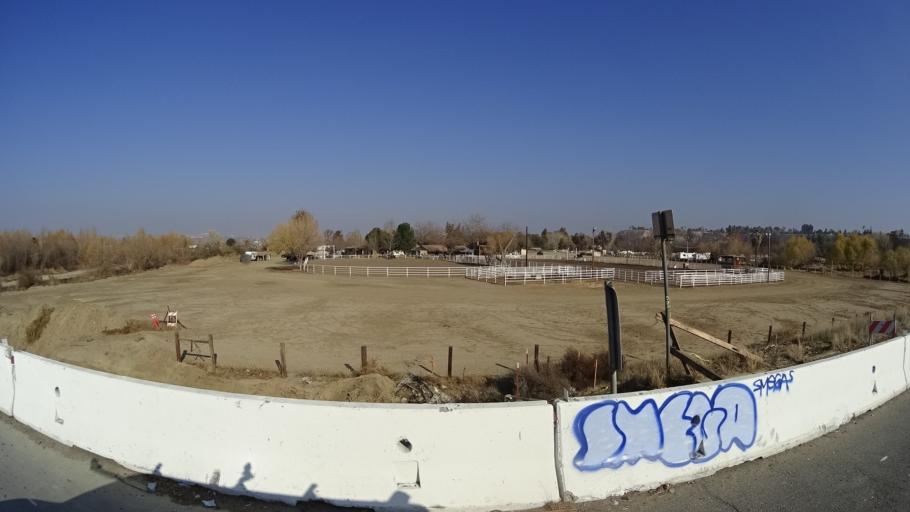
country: US
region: California
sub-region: Kern County
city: Oildale
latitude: 35.4070
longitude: -119.0093
